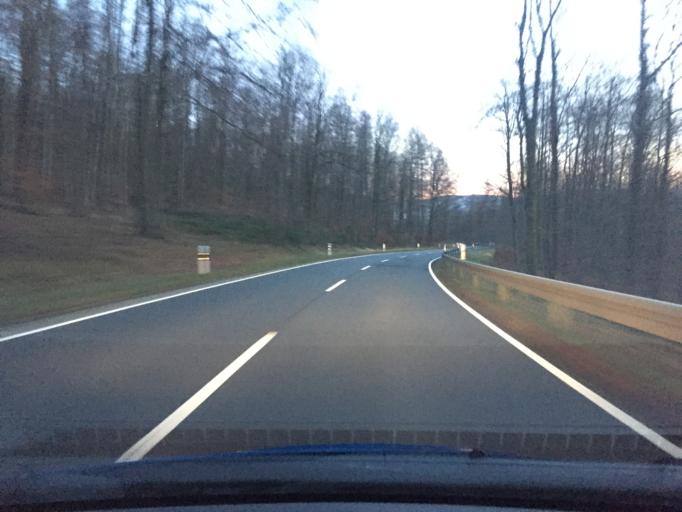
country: DE
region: Lower Saxony
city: Luerdissen
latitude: 51.9632
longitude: 9.6408
